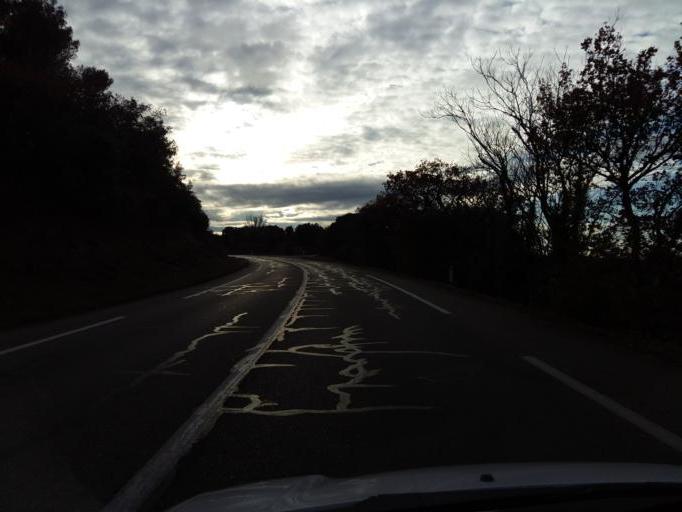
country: FR
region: Provence-Alpes-Cote d'Azur
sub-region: Departement du Vaucluse
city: Visan
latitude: 44.3493
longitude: 4.9570
